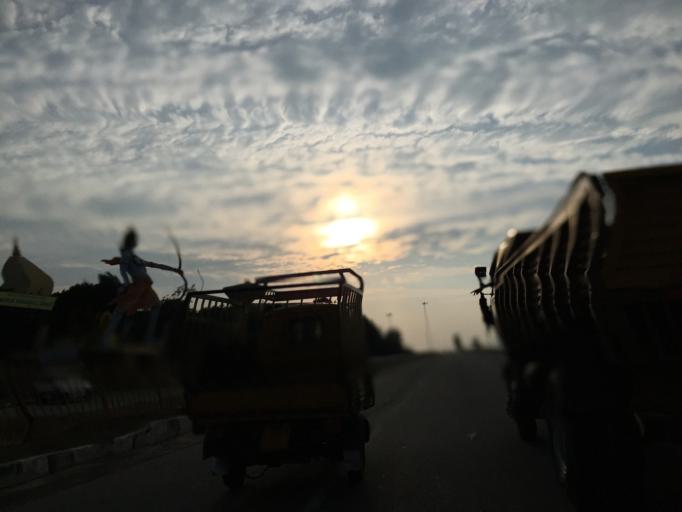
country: IN
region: Karnataka
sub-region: Kolar
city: Kolar
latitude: 13.1337
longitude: 78.1761
